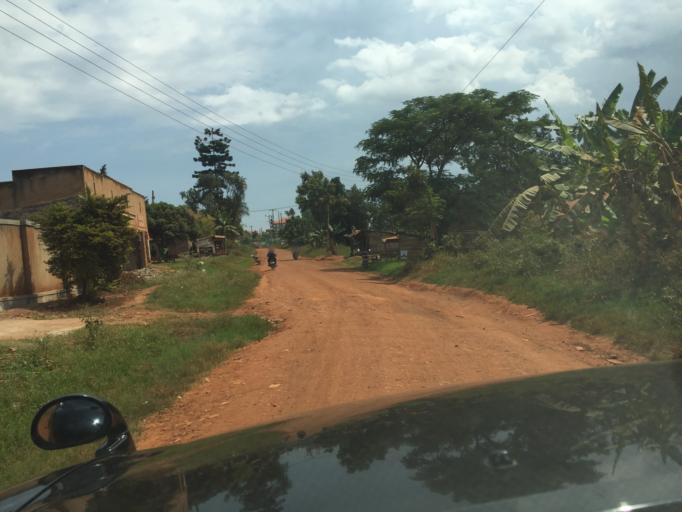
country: UG
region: Central Region
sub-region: Wakiso District
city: Kireka
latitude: 0.4109
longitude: 32.6204
